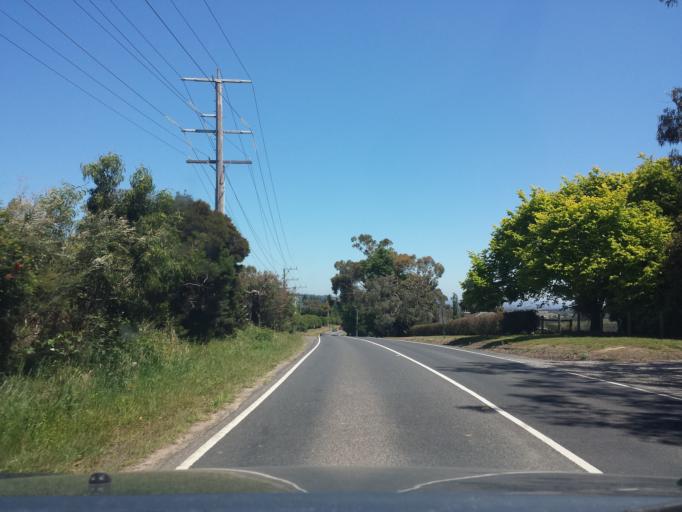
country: AU
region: Victoria
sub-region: Yarra Ranges
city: Belgrave South
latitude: -37.9410
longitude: 145.3565
